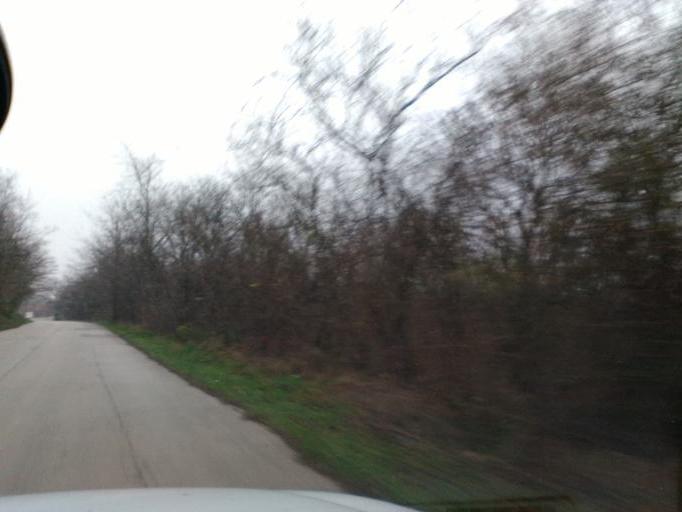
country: HU
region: Pest
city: Soskut
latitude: 47.4003
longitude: 18.7870
